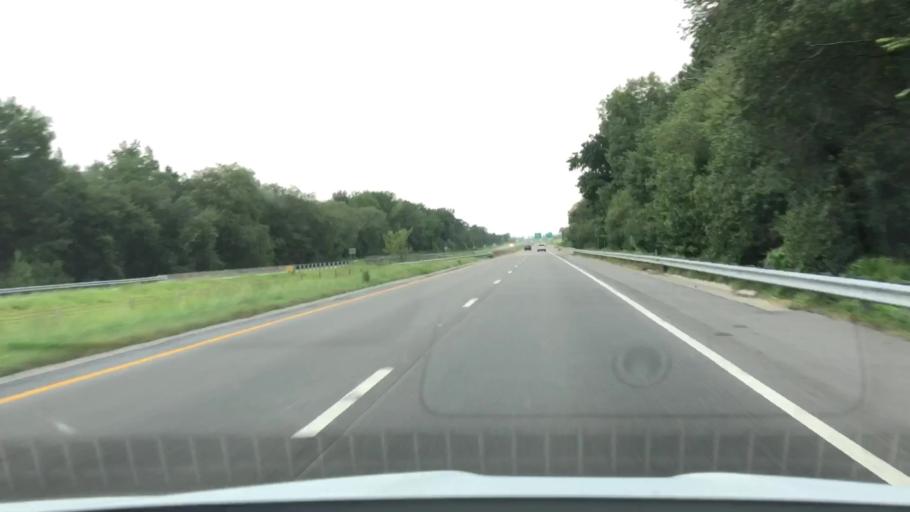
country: US
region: North Carolina
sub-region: Lenoir County
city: La Grange
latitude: 35.2959
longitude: -77.8061
